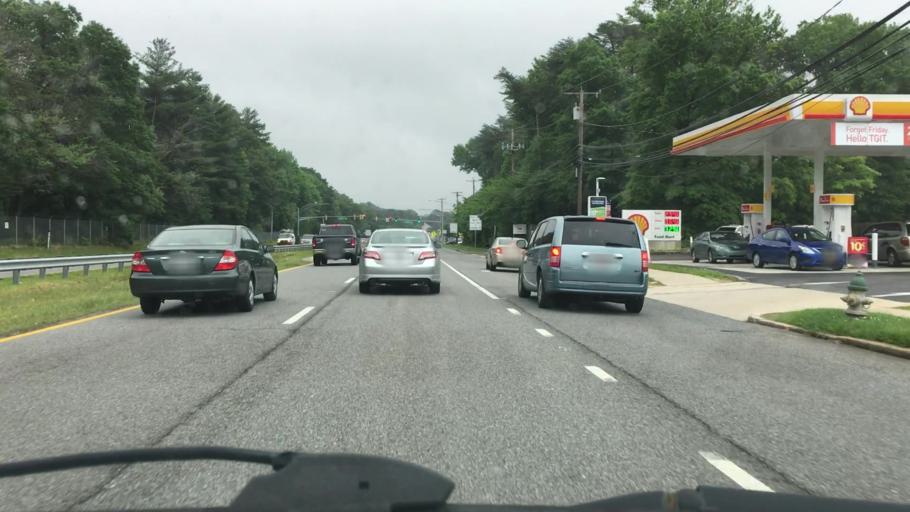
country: US
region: Maryland
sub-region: Prince George's County
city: Goddard
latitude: 38.9912
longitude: -76.8581
